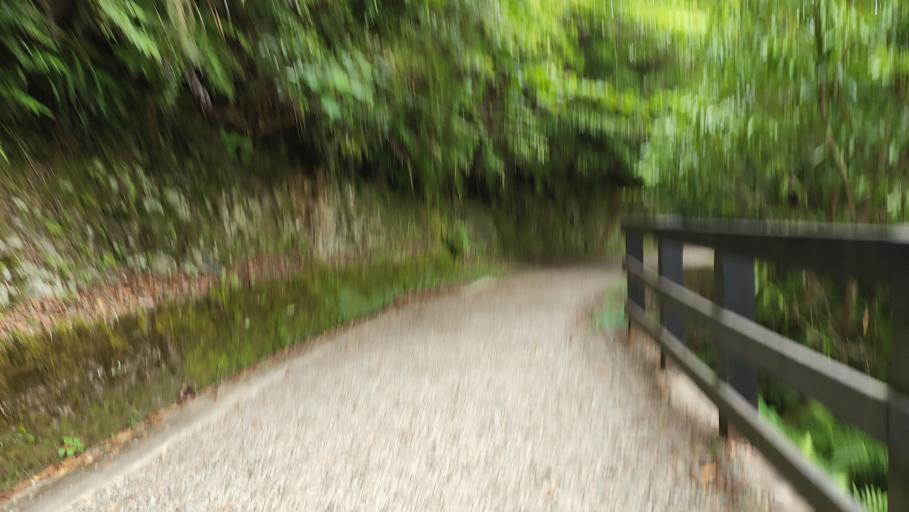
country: TW
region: Taiwan
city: Daxi
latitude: 24.7104
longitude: 121.4348
